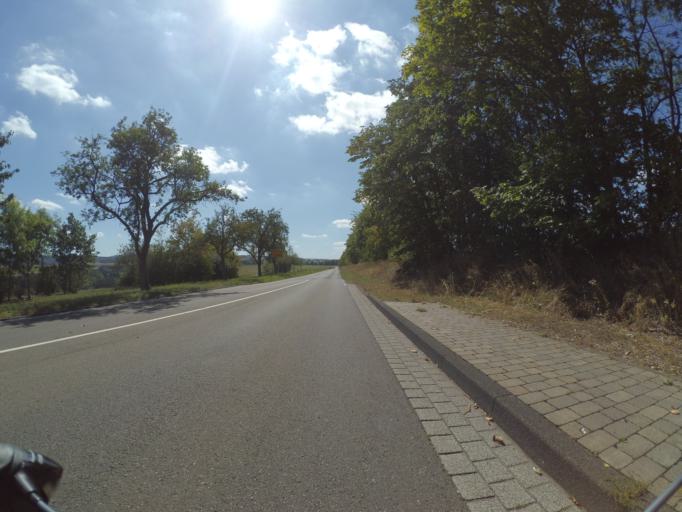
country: DE
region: Rheinland-Pfalz
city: Thomm
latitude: 49.7375
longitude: 6.8045
